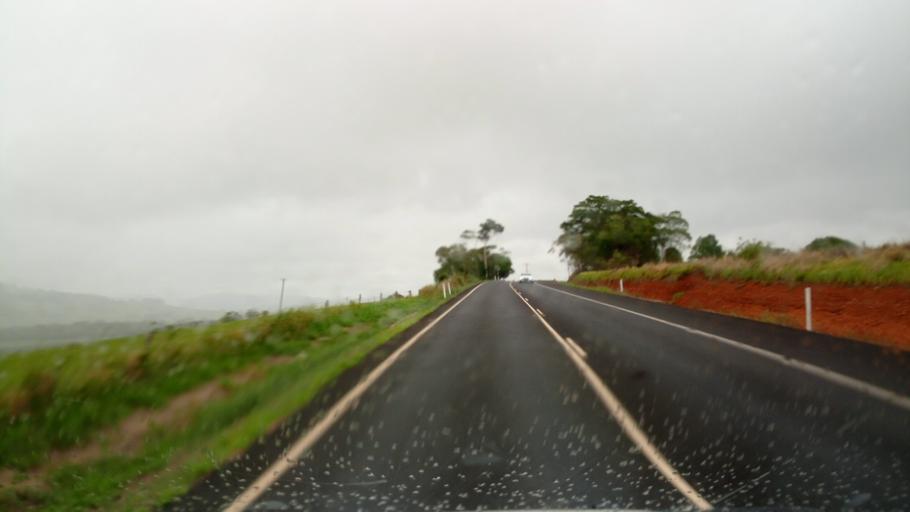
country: AU
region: Queensland
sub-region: Tablelands
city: Atherton
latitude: -17.2810
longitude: 145.5973
